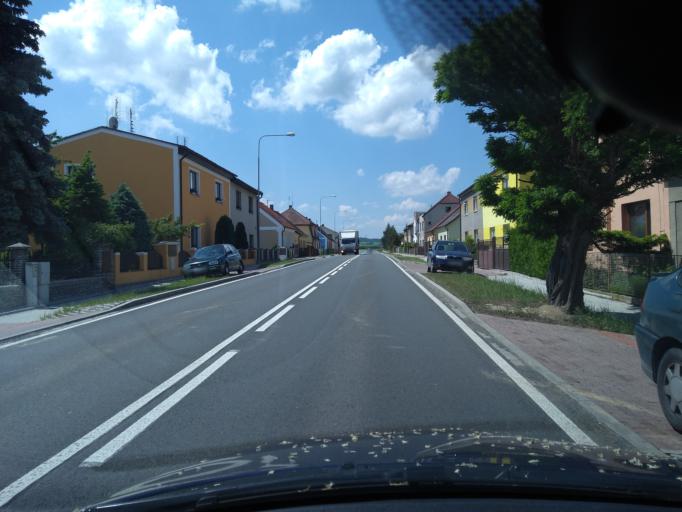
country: CZ
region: Plzensky
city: Prestice
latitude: 49.5435
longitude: 13.3133
